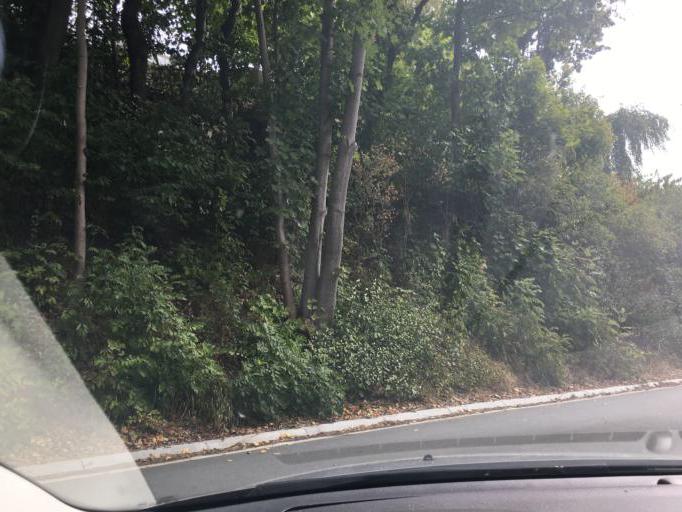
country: DE
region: Thuringia
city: Birkenhugel
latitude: 50.5002
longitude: 11.7363
